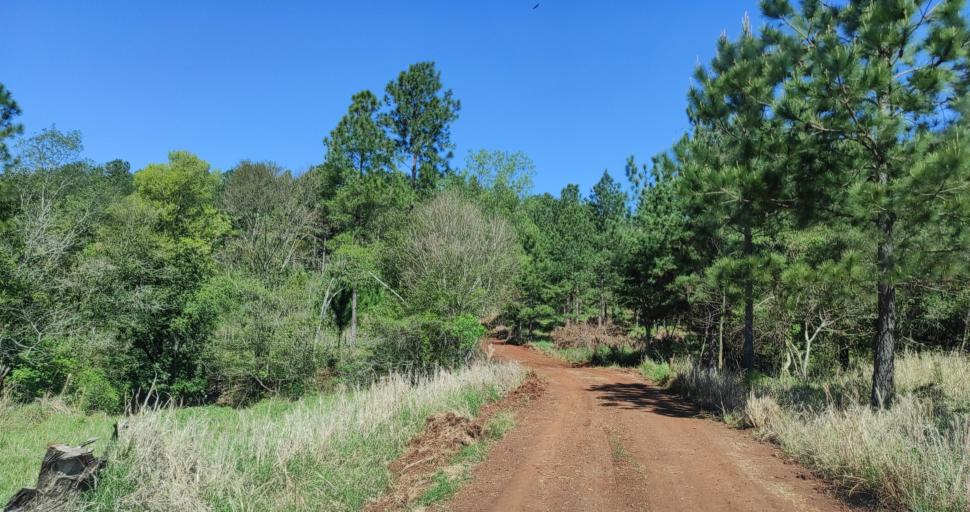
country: AR
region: Misiones
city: Ruiz de Montoya
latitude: -26.9420
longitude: -54.9805
